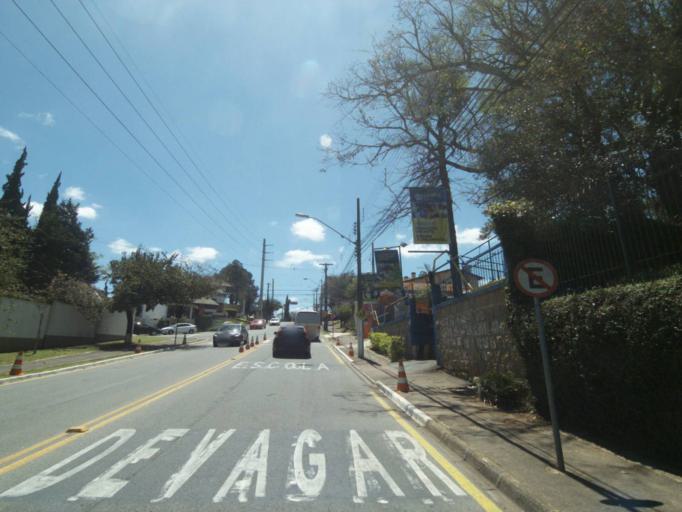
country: BR
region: Parana
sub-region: Curitiba
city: Curitiba
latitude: -25.3901
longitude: -49.2723
